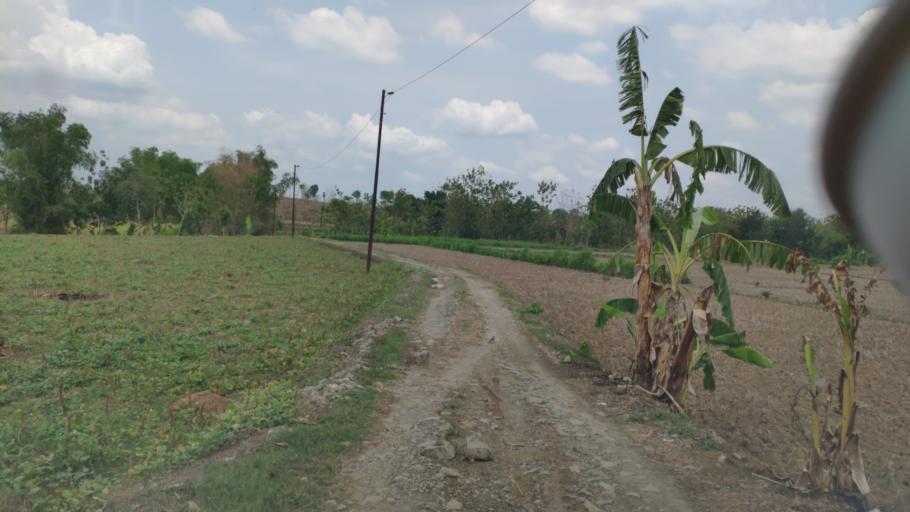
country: ID
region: Central Java
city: Gumiring
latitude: -7.0486
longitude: 111.3940
